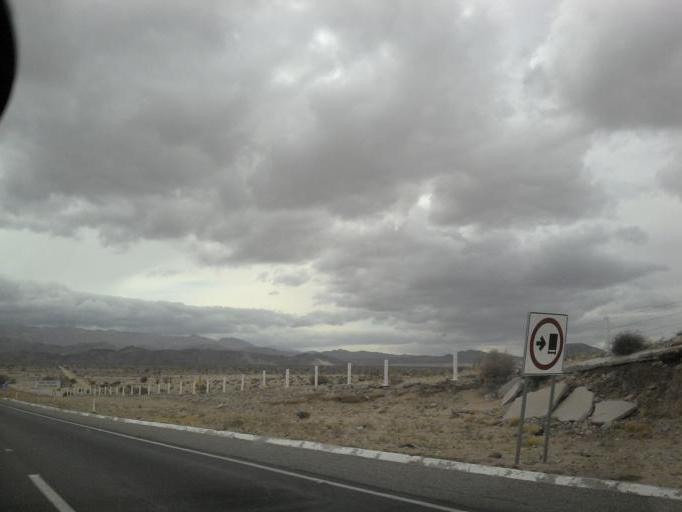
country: MX
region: Baja California
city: Progreso
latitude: 32.5647
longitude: -115.8772
